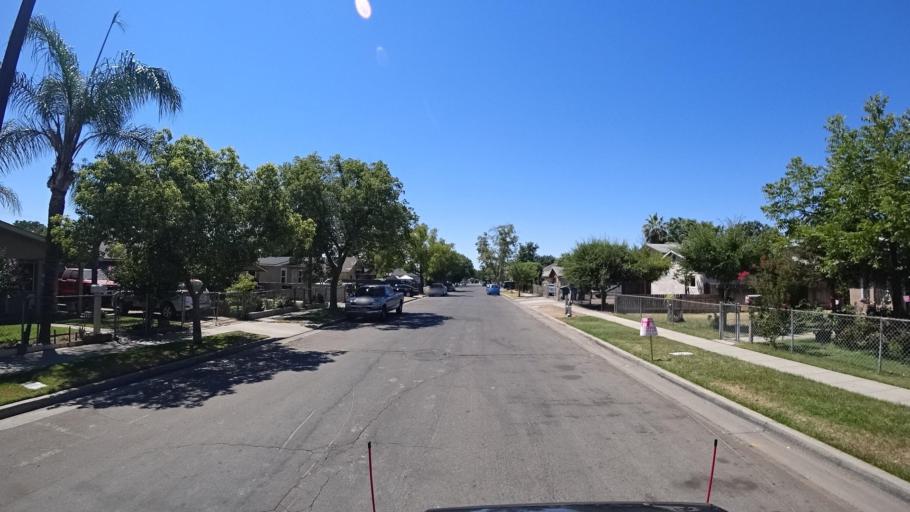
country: US
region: California
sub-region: Fresno County
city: Fresno
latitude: 36.7380
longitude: -119.7416
